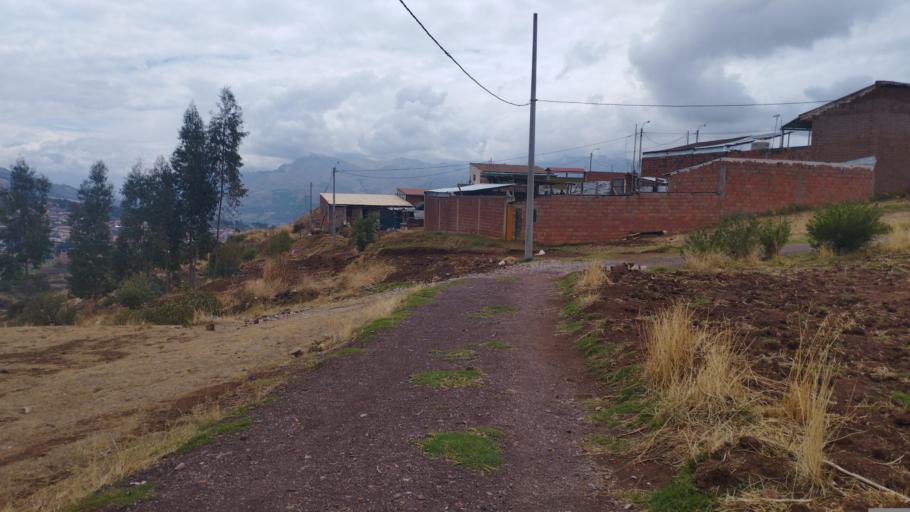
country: PE
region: Cusco
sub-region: Provincia de Cusco
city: Cusco
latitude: -13.5188
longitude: -71.9138
